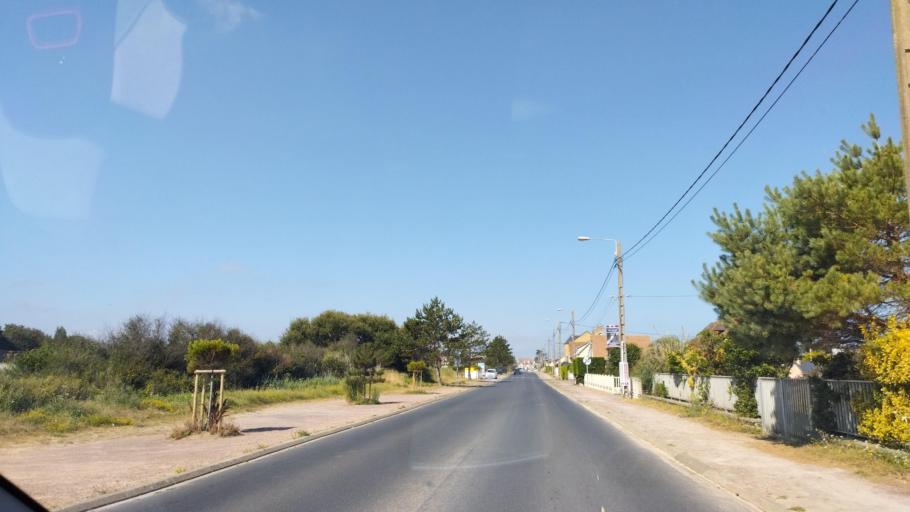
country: FR
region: Lower Normandy
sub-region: Departement du Calvados
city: Bernieres-sur-Mer
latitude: 49.3344
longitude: -0.4109
